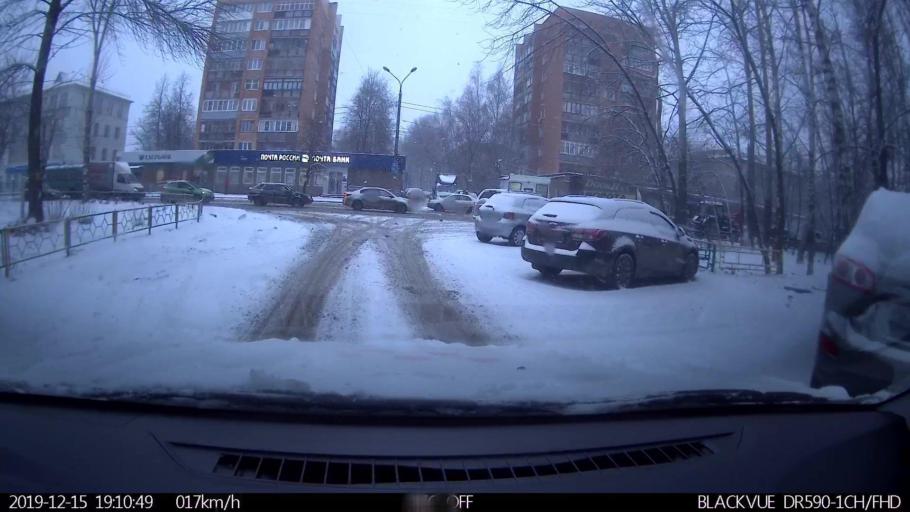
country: RU
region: Nizjnij Novgorod
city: Gorbatovka
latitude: 56.3438
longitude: 43.8390
